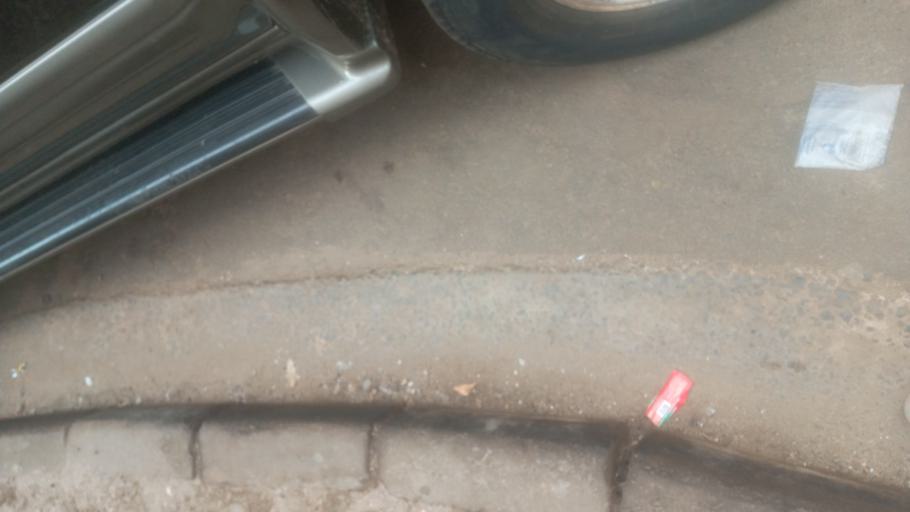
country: SL
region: Western Area
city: Freetown
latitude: 8.4749
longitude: -13.2410
